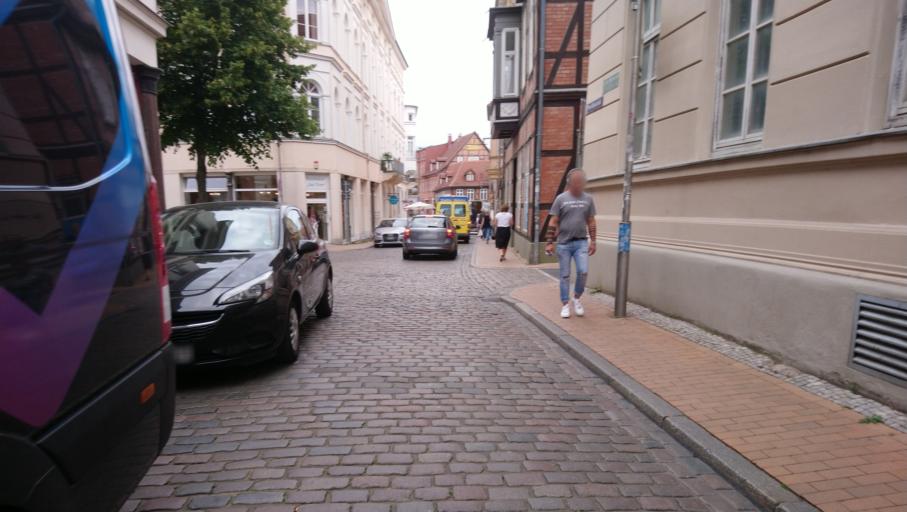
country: DE
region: Mecklenburg-Vorpommern
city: Altstadt
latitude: 53.6292
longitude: 11.4155
